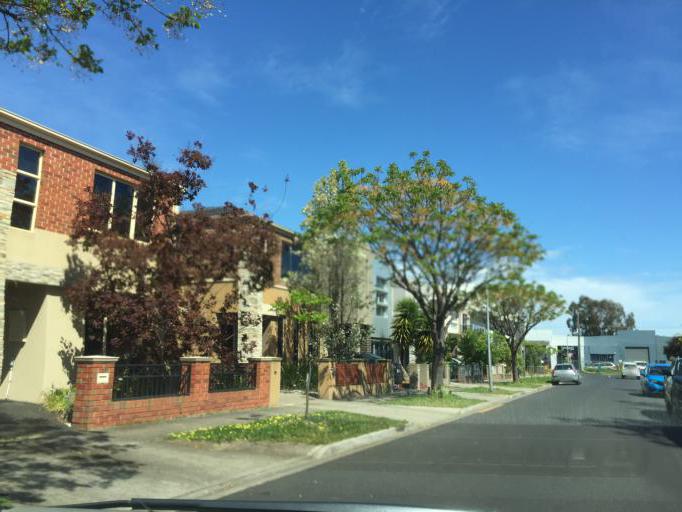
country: AU
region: Victoria
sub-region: Maribyrnong
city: Maribyrnong
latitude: -37.7856
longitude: 144.8859
